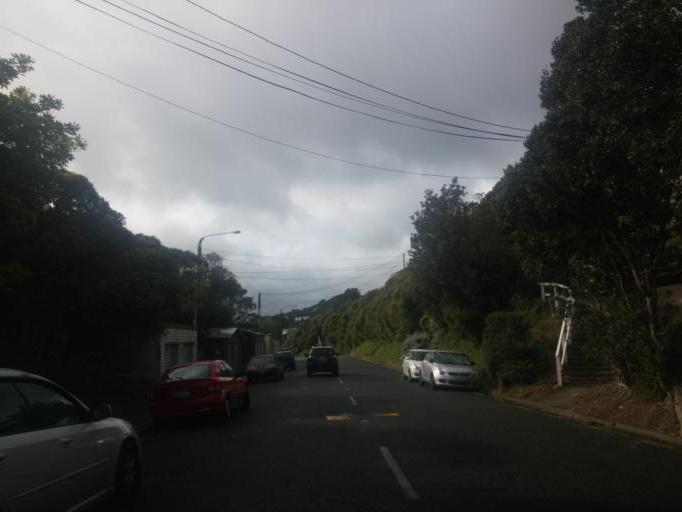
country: NZ
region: Wellington
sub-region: Wellington City
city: Kelburn
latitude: -41.2721
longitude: 174.7584
